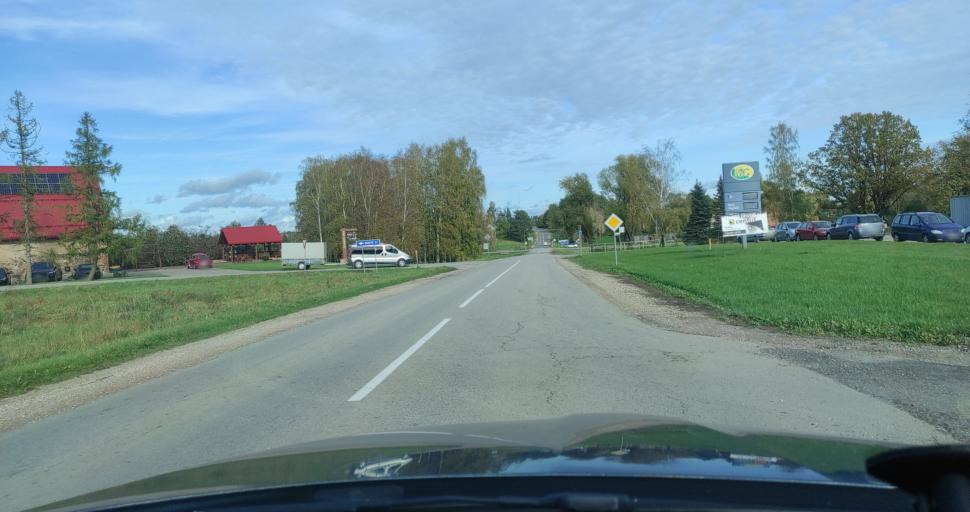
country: LV
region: Jaunpils
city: Jaunpils
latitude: 56.7292
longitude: 23.0106
